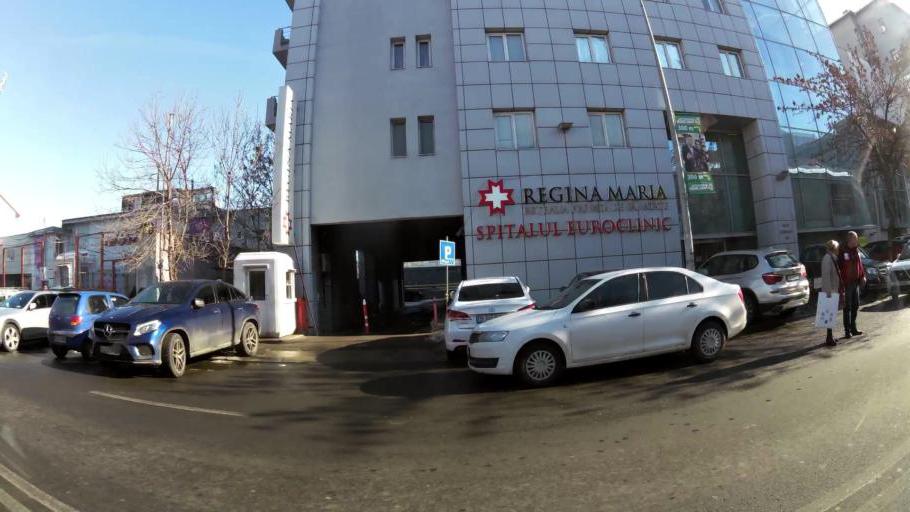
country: RO
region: Bucuresti
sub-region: Municipiul Bucuresti
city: Bucharest
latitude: 44.4546
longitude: 26.1008
